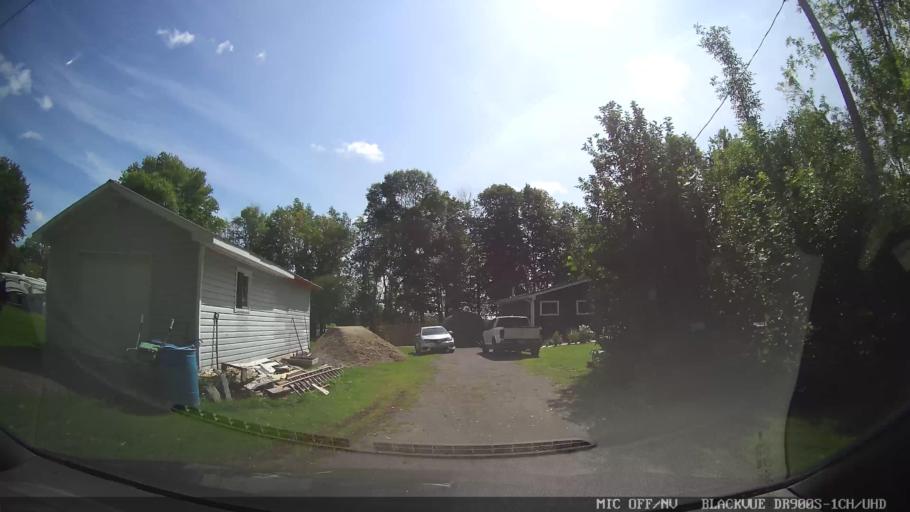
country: CA
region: Ontario
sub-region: Lanark County
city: Smiths Falls
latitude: 45.0083
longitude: -75.7525
